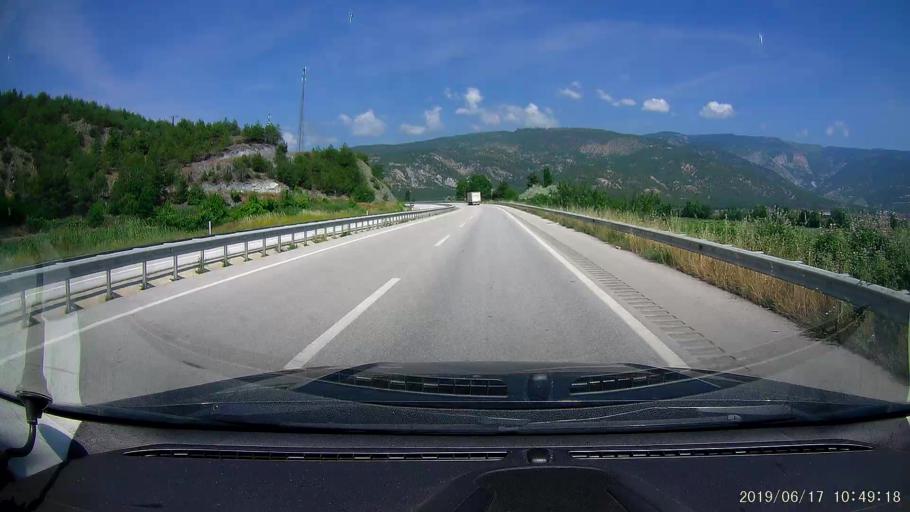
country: TR
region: Corum
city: Hacihamza
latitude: 41.1004
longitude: 34.4131
